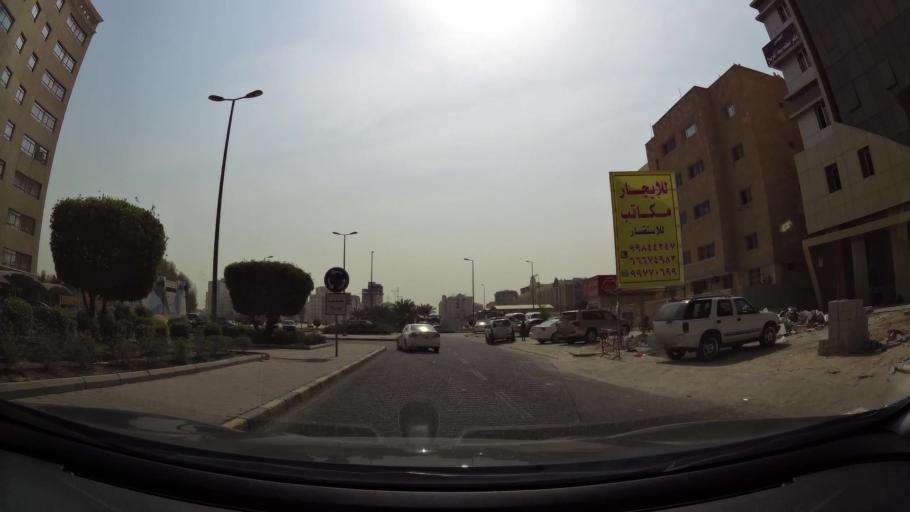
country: KW
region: Al Asimah
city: Ar Rabiyah
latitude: 29.3063
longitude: 47.9149
